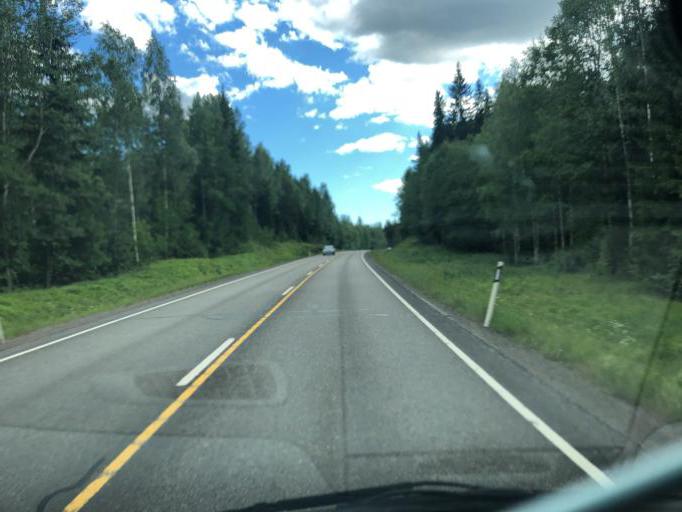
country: FI
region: Kymenlaakso
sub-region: Kouvola
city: Kouvola
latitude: 61.0096
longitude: 26.9492
